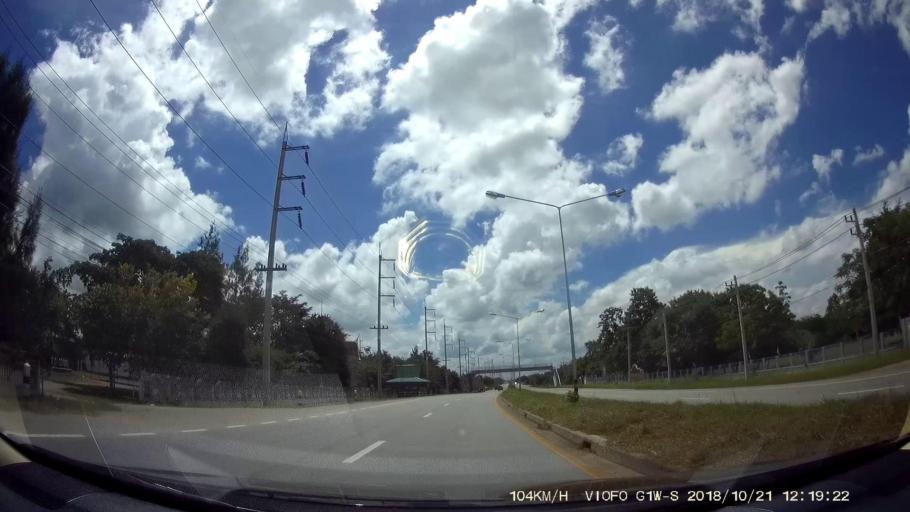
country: TH
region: Nakhon Ratchasima
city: Dan Khun Thot
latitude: 15.3018
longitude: 101.8139
